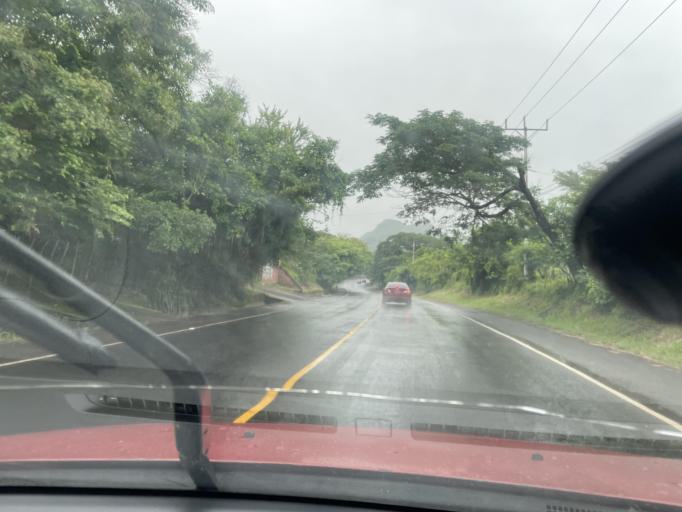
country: SV
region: San Miguel
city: San Miguel
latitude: 13.5571
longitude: -88.1116
